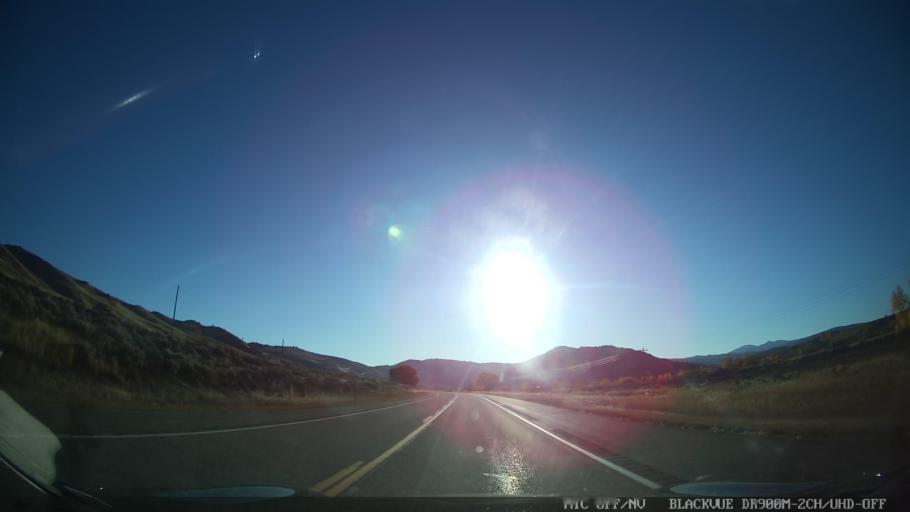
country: US
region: Colorado
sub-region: Grand County
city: Hot Sulphur Springs
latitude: 40.0518
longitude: -106.1581
